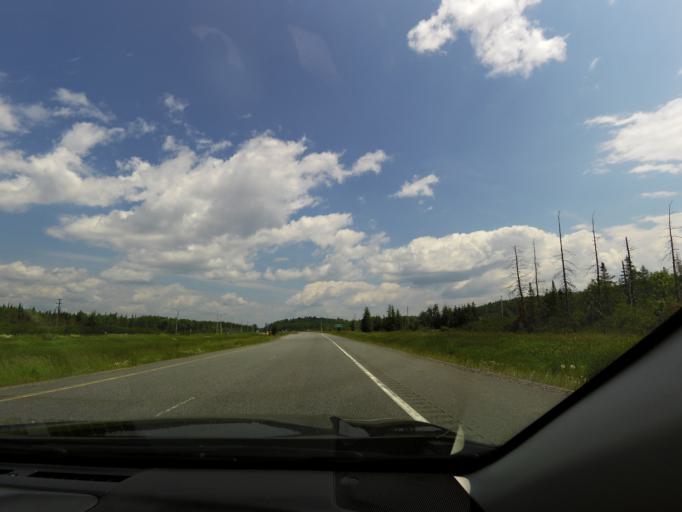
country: CA
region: Ontario
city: Huntsville
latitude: 45.2349
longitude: -79.3028
